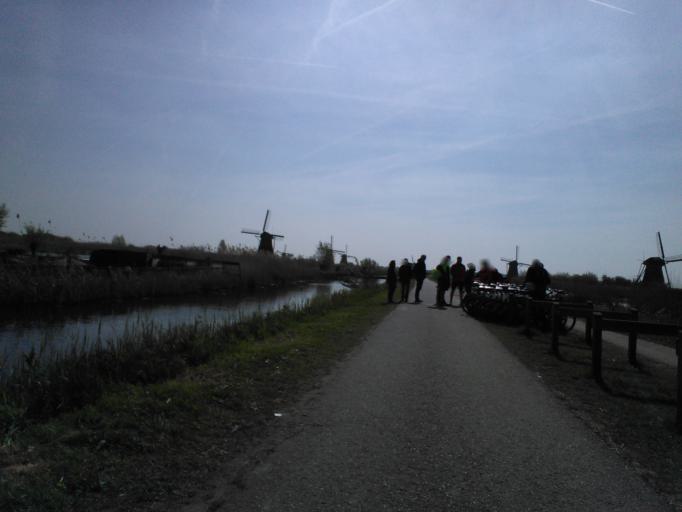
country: NL
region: South Holland
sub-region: Gemeente Alblasserdam
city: Alblasserdam
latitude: 51.8834
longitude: 4.6417
